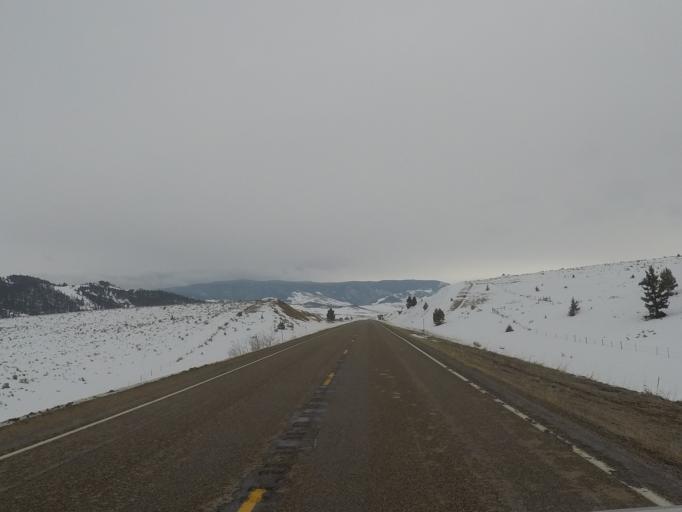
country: US
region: Montana
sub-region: Meagher County
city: White Sulphur Springs
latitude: 46.6229
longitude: -110.8470
